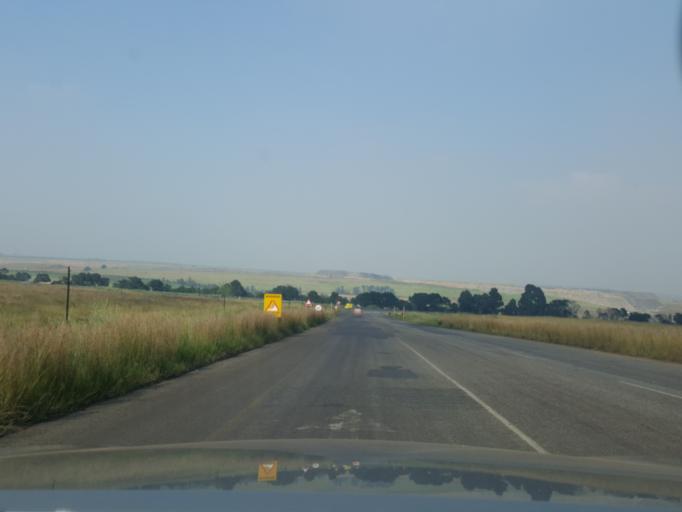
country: ZA
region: Mpumalanga
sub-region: Nkangala District Municipality
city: Witbank
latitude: -26.0169
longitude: 29.3156
